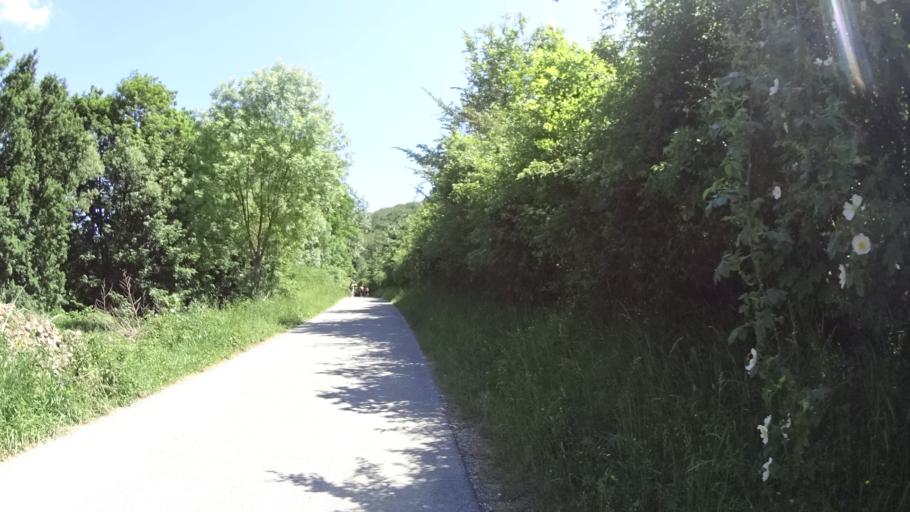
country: DE
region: Bavaria
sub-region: Regierungsbezirk Mittelfranken
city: Adelshofen
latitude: 49.3991
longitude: 10.1575
